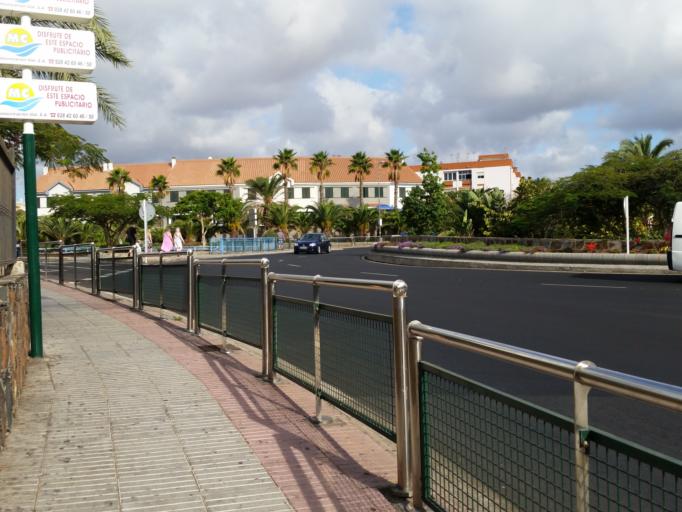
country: ES
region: Canary Islands
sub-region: Provincia de Las Palmas
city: Playa del Ingles
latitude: 27.7634
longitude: -15.5790
